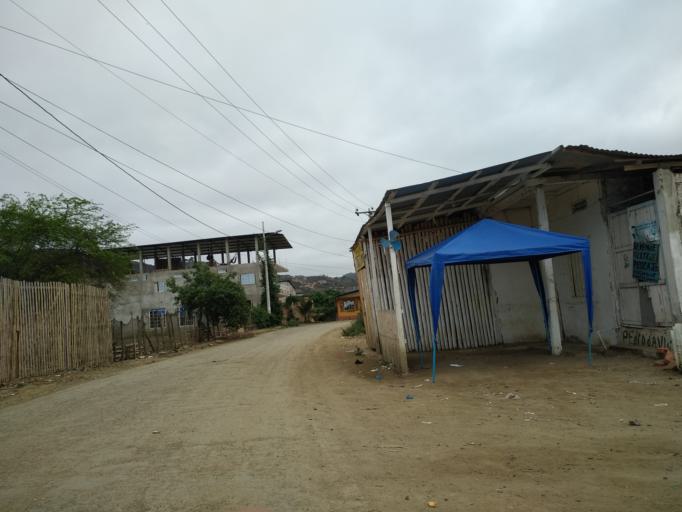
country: EC
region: Manabi
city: Jipijapa
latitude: -1.5522
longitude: -80.8098
